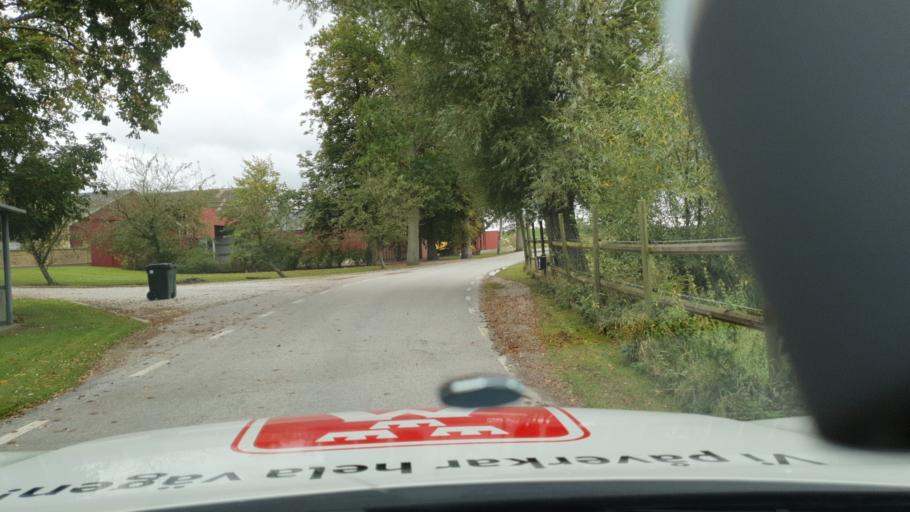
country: SE
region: Skane
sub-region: Svedala Kommun
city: Svedala
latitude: 55.4967
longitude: 13.1853
